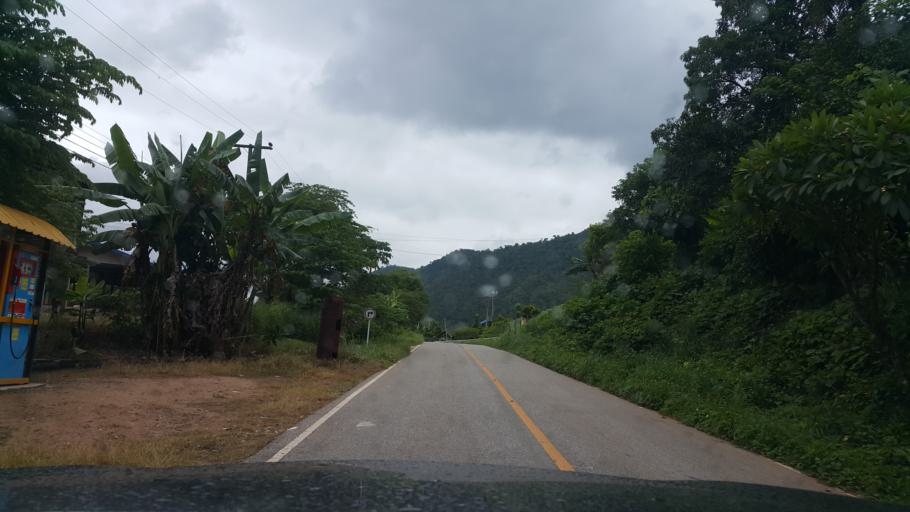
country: TH
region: Loei
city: Na Haeo
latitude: 17.5376
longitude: 100.8339
